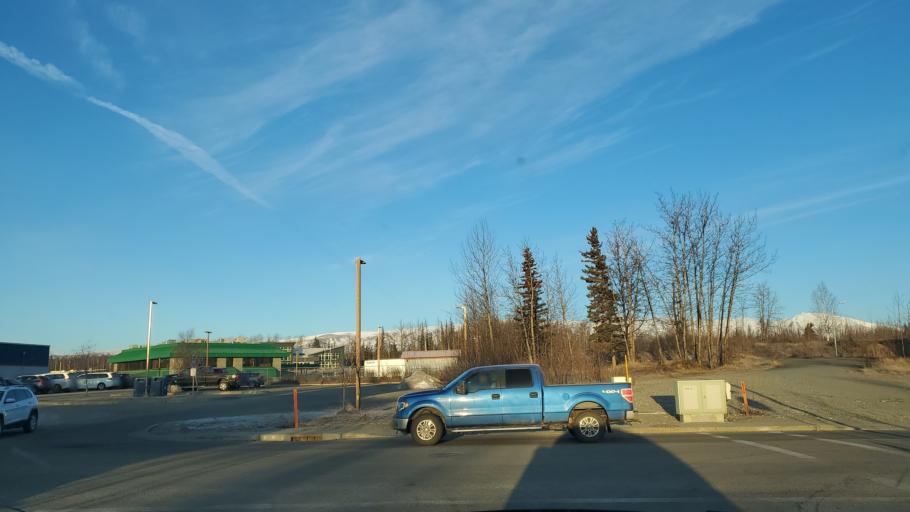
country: US
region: Alaska
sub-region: Matanuska-Susitna Borough
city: Wasilla
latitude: 61.5830
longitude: -149.4393
